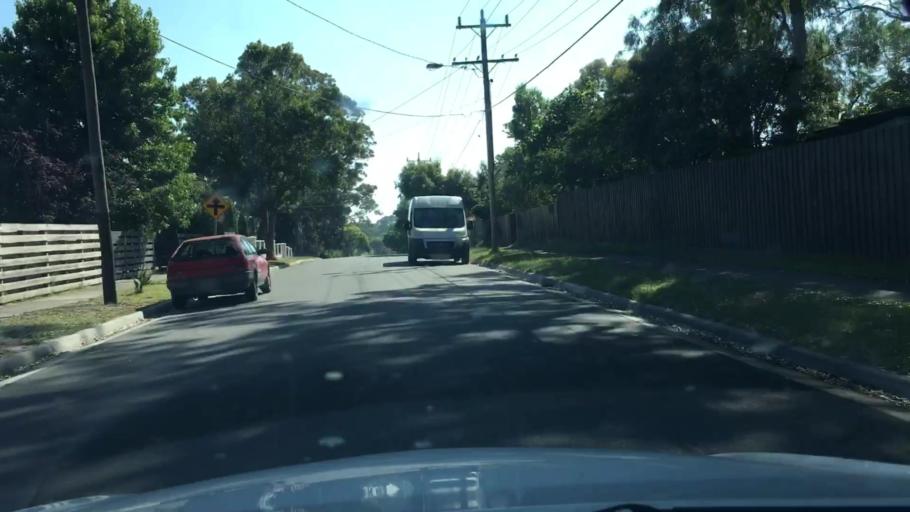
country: AU
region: Victoria
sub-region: Greater Dandenong
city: Noble Park
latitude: -37.9562
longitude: 145.1749
